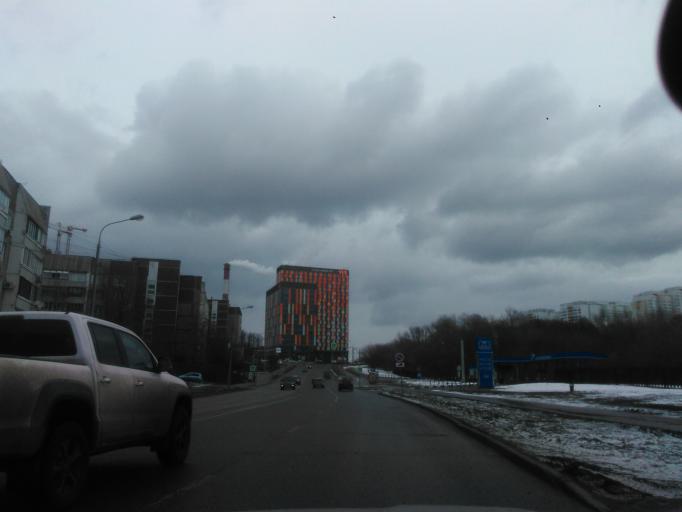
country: RU
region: Moskovskaya
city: Pavshino
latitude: 55.8399
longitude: 37.3672
